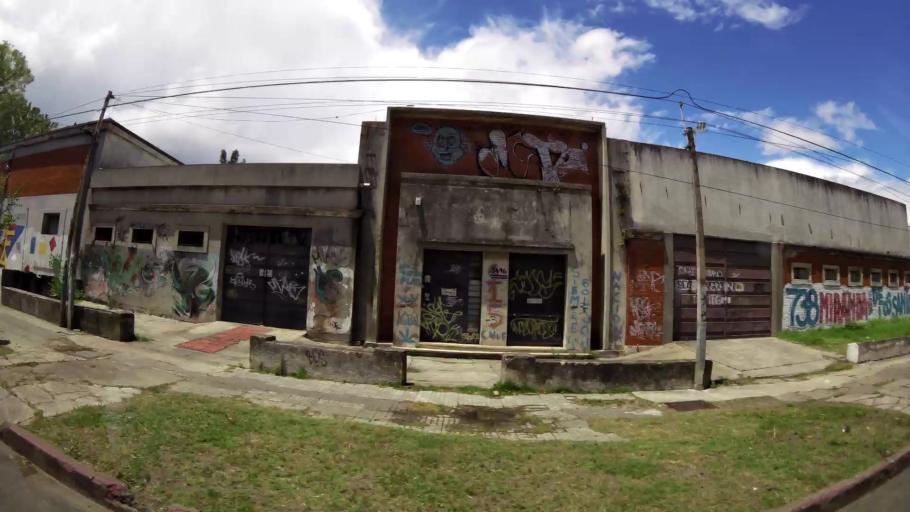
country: UY
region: Montevideo
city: Montevideo
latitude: -34.8590
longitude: -56.1850
